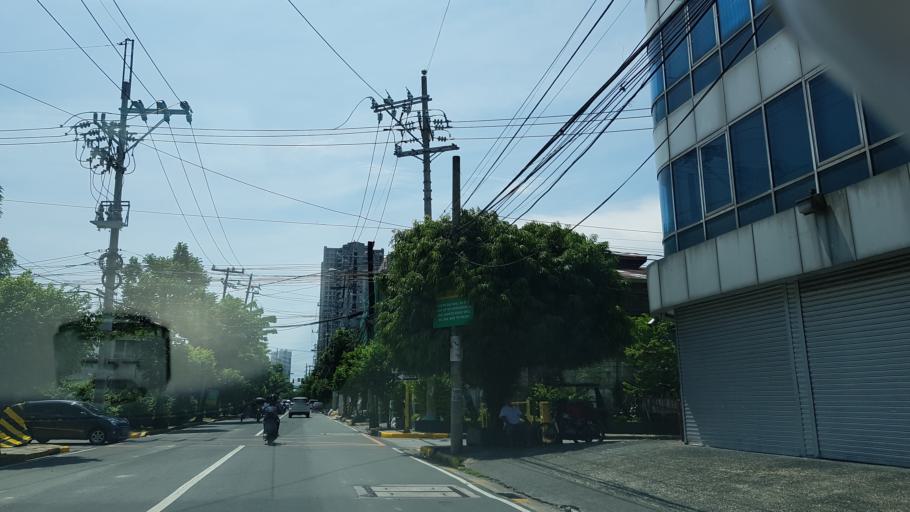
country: PH
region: Metro Manila
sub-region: Makati City
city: Makati City
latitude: 14.5665
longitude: 121.0165
